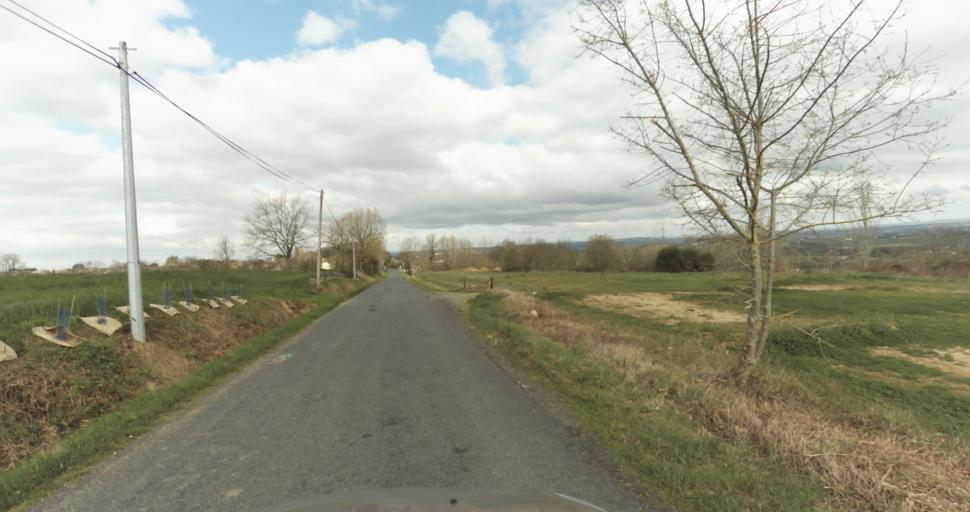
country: FR
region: Midi-Pyrenees
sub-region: Departement du Tarn
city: Frejairolles
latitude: 43.8682
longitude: 2.2022
